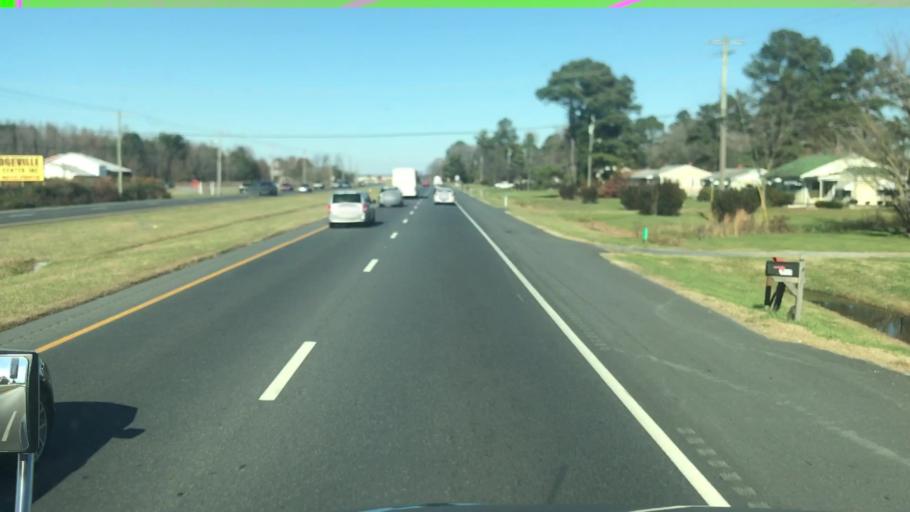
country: US
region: Delaware
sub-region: Sussex County
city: Bridgeville
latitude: 38.7028
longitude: -75.5886
